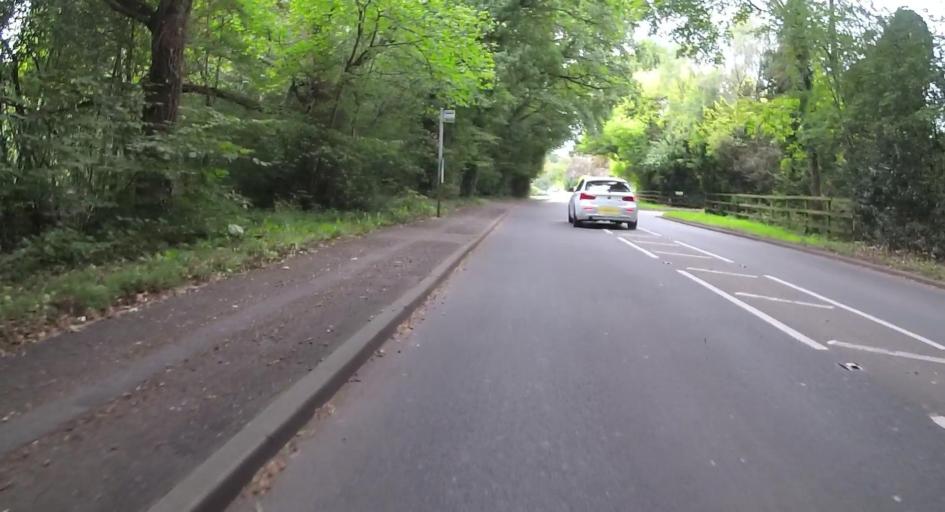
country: GB
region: England
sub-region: Surrey
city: Knaphill
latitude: 51.3269
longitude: -0.5923
